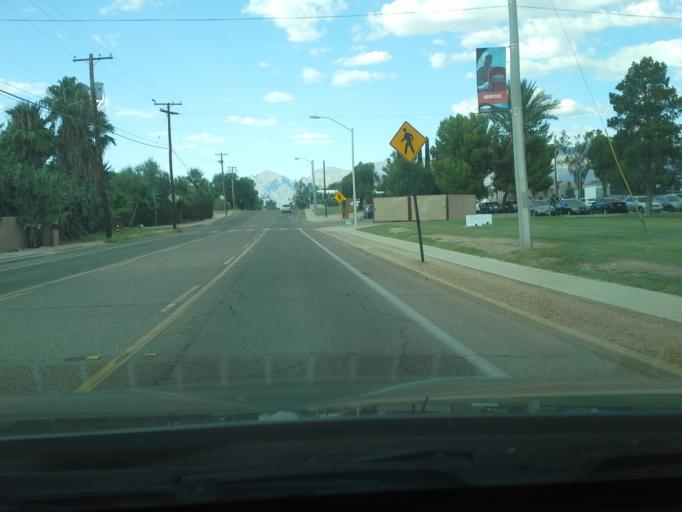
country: US
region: Arizona
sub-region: Pima County
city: Tucson
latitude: 32.2332
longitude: -110.9353
